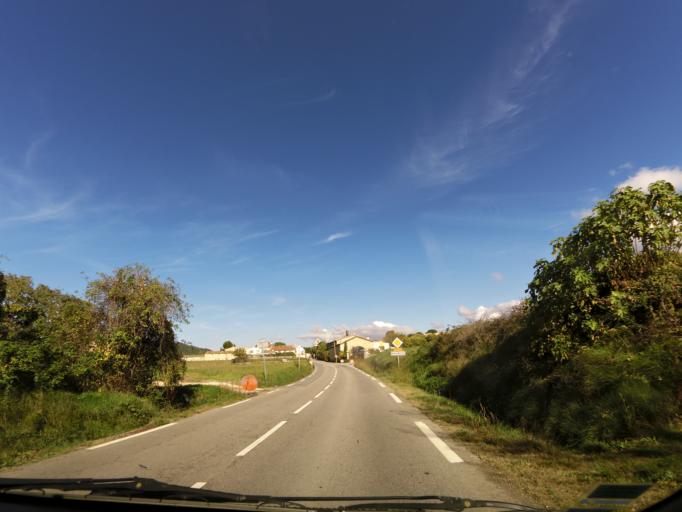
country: FR
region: Languedoc-Roussillon
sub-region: Departement du Gard
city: Saint-Mamert-du-Gard
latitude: 43.8967
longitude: 4.1016
